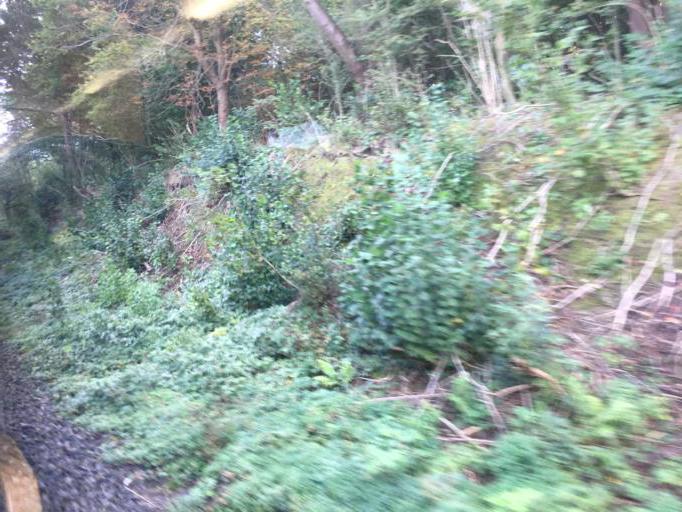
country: DE
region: Schleswig-Holstein
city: Kronshagen
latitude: 54.3133
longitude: 10.0841
